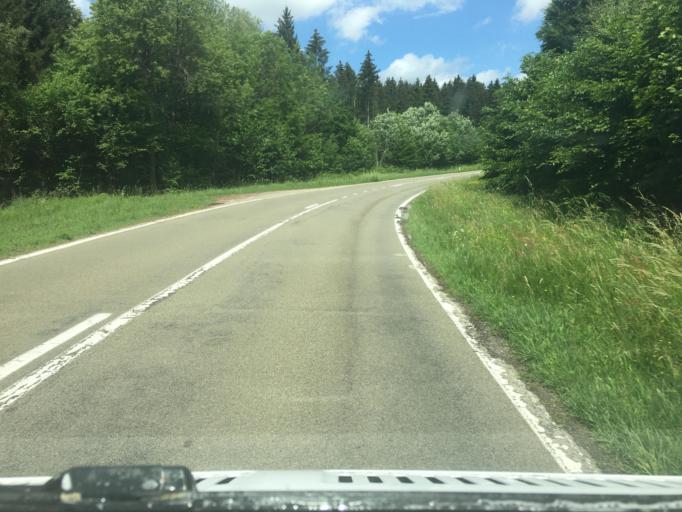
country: BE
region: Wallonia
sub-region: Province du Luxembourg
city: Florenville
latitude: 49.6647
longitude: 5.3304
